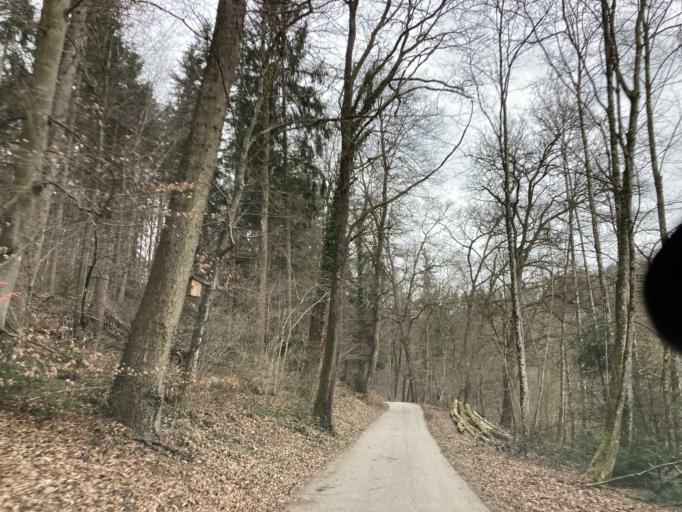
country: DE
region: Baden-Wuerttemberg
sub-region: Tuebingen Region
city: Hirrlingen
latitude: 48.4300
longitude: 8.8602
